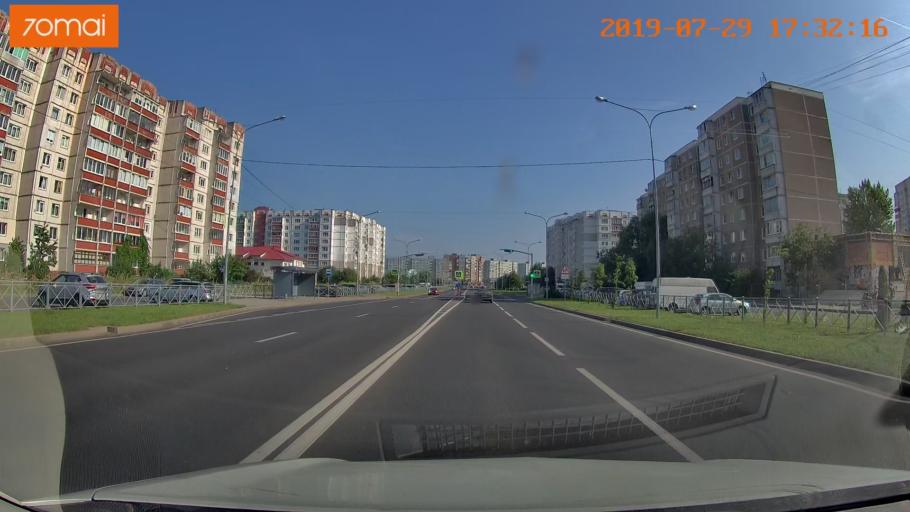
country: RU
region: Kaliningrad
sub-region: Gorod Kaliningrad
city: Kaliningrad
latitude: 54.7440
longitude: 20.4918
